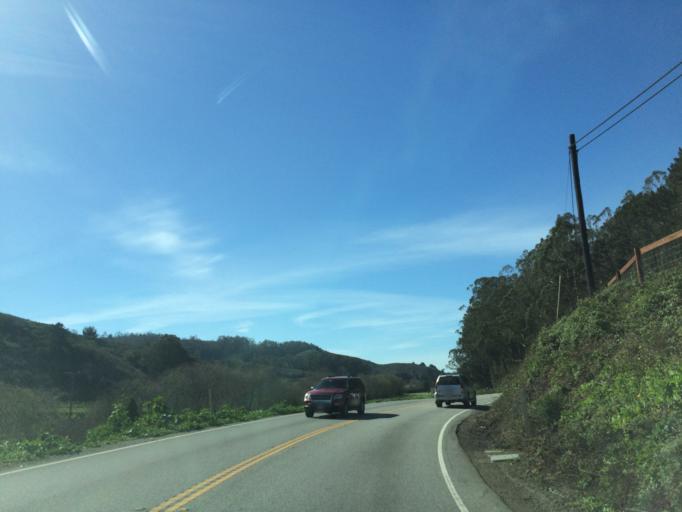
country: US
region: California
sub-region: San Mateo County
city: Half Moon Bay
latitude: 37.4827
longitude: -122.4015
